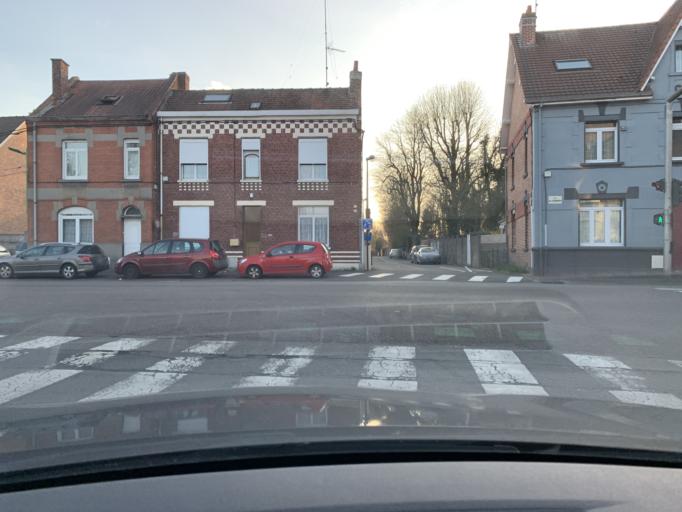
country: FR
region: Nord-Pas-de-Calais
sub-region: Departement du Nord
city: Douai
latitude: 50.3586
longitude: 3.0807
